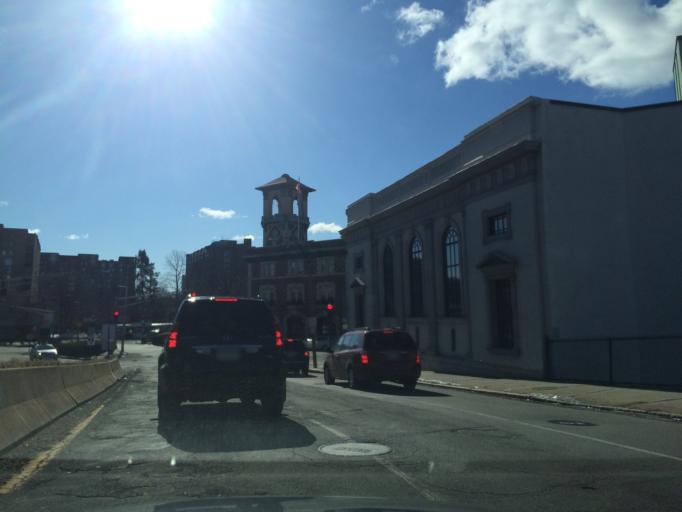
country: US
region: Massachusetts
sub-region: Norfolk County
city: Brookline
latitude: 42.3320
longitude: -71.1181
